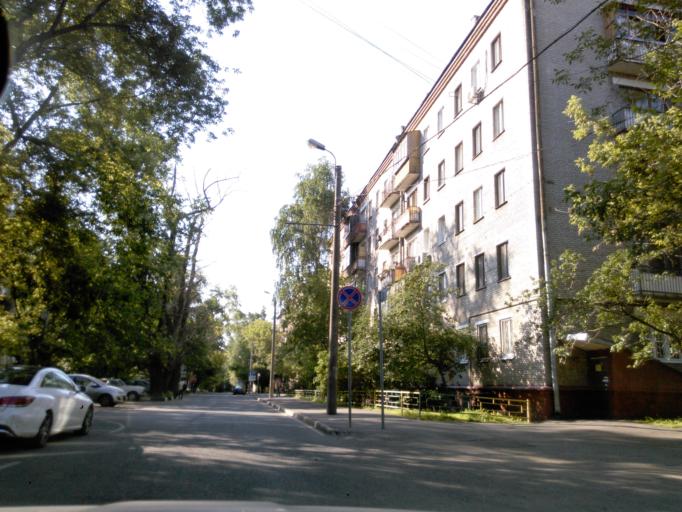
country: RU
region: Moskovskaya
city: Dorogomilovo
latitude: 55.7782
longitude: 37.5718
